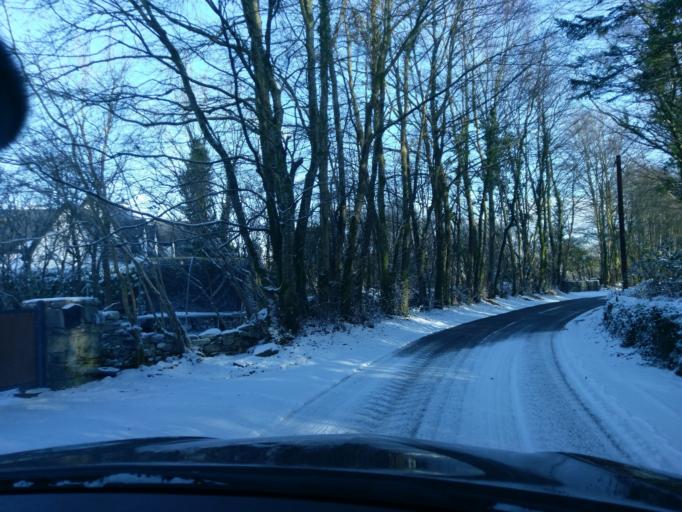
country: IE
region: Connaught
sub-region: County Galway
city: Gort
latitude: 53.1828
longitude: -8.8073
